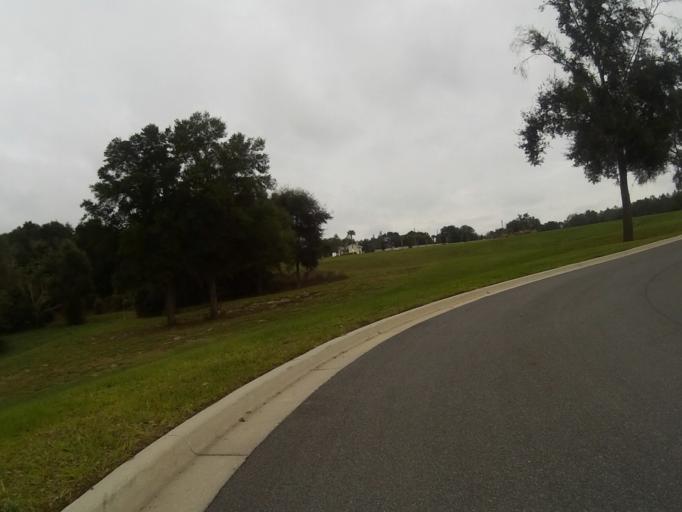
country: US
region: Florida
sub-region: Lake County
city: Umatilla
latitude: 28.9619
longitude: -81.6534
